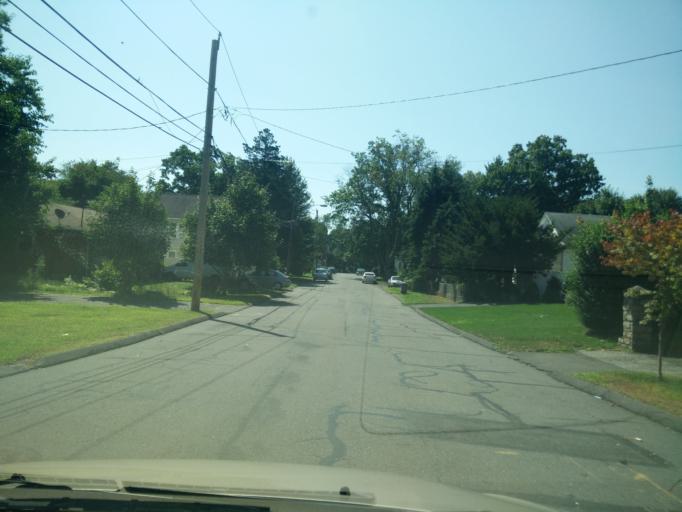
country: US
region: Connecticut
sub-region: Fairfield County
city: Bridgeport
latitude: 41.1732
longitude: -73.2334
